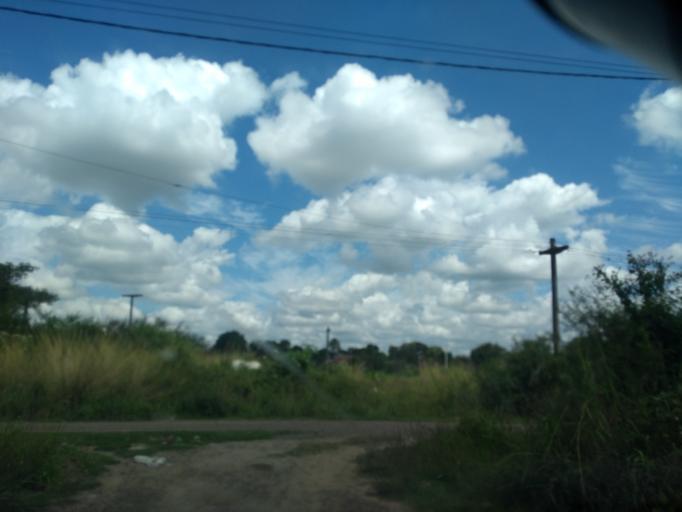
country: AR
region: Chaco
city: Fontana
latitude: -27.4051
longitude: -59.0397
